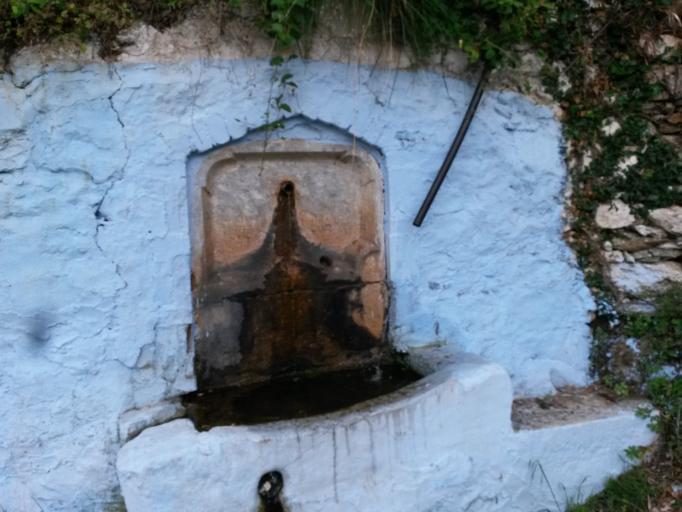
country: GR
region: North Aegean
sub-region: Nomos Lesvou
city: Agiasos
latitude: 39.0994
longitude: 26.3916
